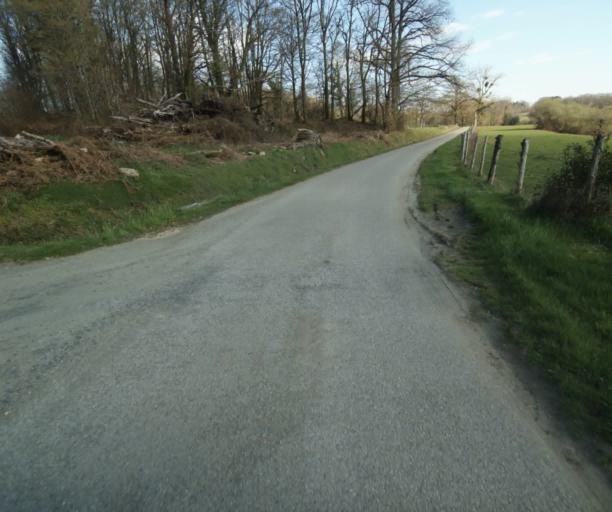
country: FR
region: Limousin
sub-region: Departement de la Correze
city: Saint-Mexant
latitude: 45.3425
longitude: 1.6025
